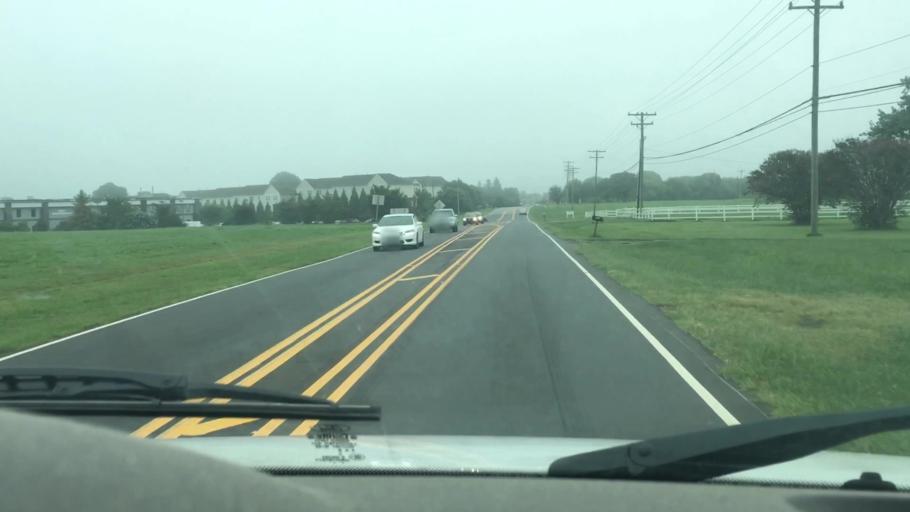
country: US
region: North Carolina
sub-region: Mecklenburg County
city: Huntersville
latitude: 35.3993
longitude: -80.7660
